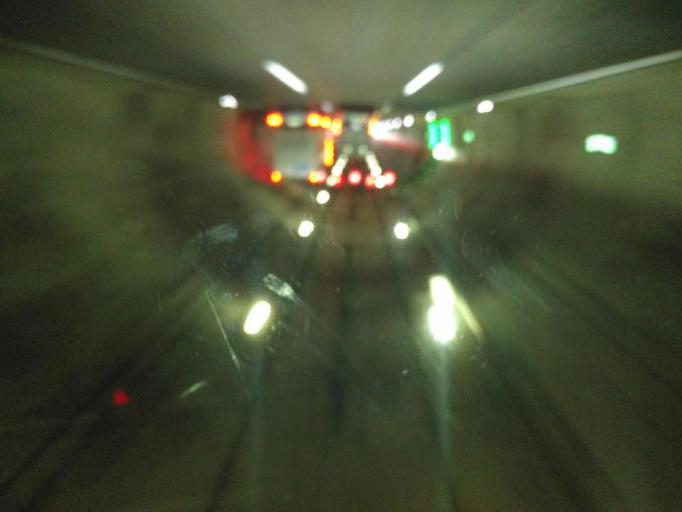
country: DE
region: Thuringia
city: Rothenstein
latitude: 50.8744
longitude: 11.5665
